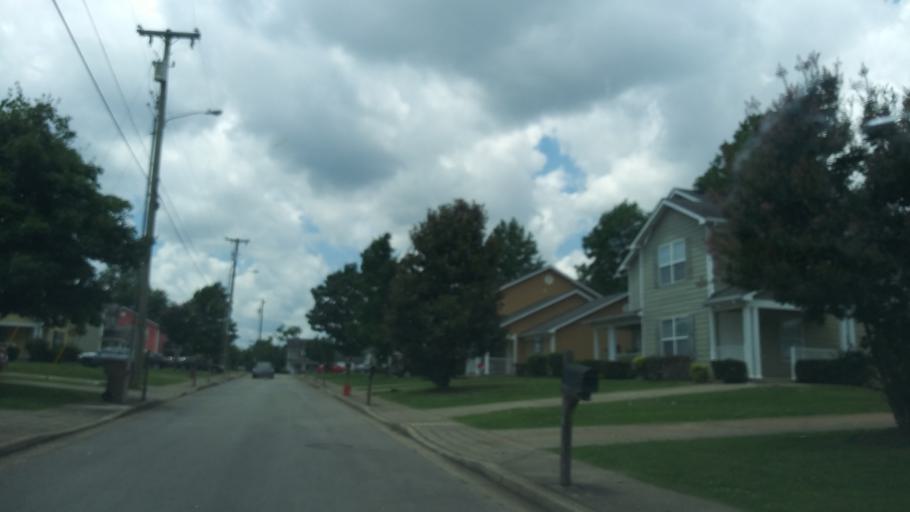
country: US
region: Tennessee
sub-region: Davidson County
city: Nashville
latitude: 36.1305
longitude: -86.7697
